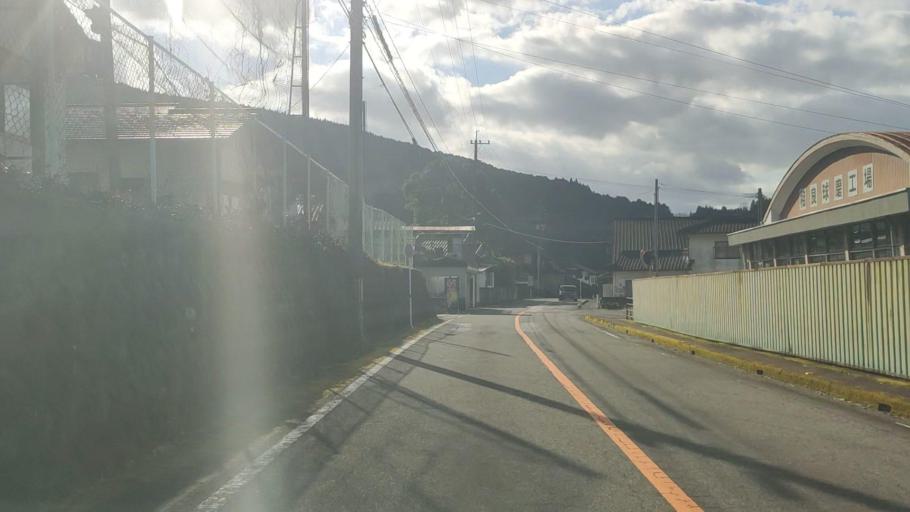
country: JP
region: Kumamoto
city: Hitoyoshi
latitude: 32.3082
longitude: 130.8478
